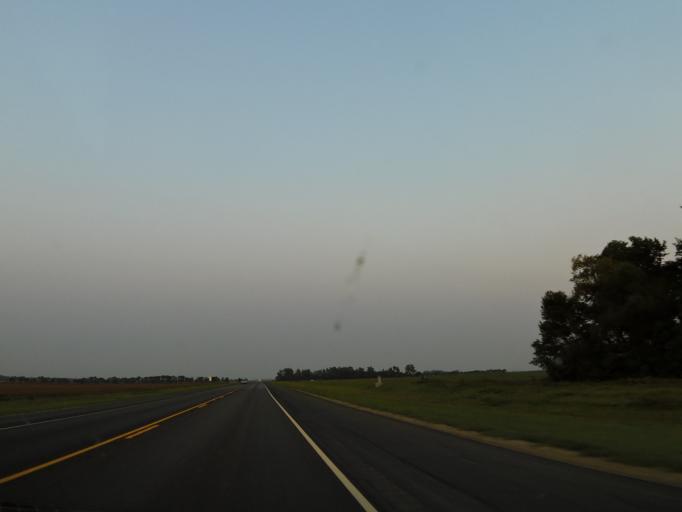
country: US
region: North Dakota
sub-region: Walsh County
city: Grafton
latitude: 48.4125
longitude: -97.5346
